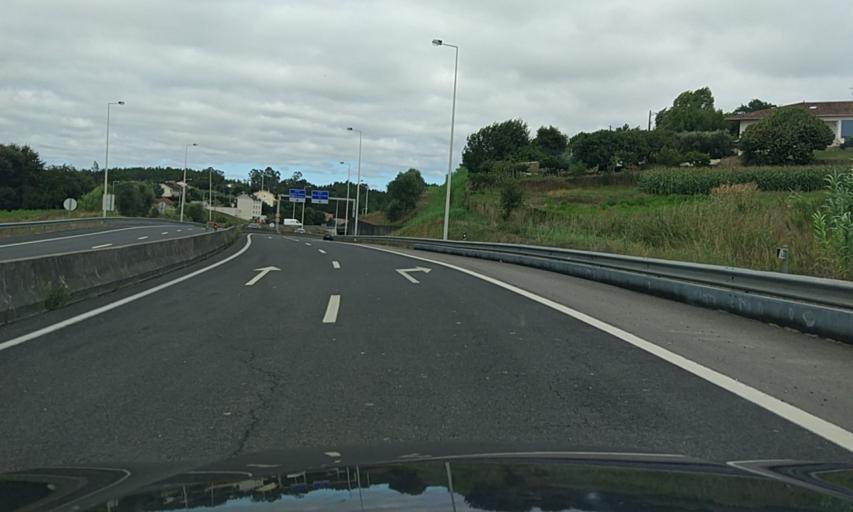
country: PT
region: Leiria
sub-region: Leiria
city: Leiria
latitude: 39.7467
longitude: -8.7773
